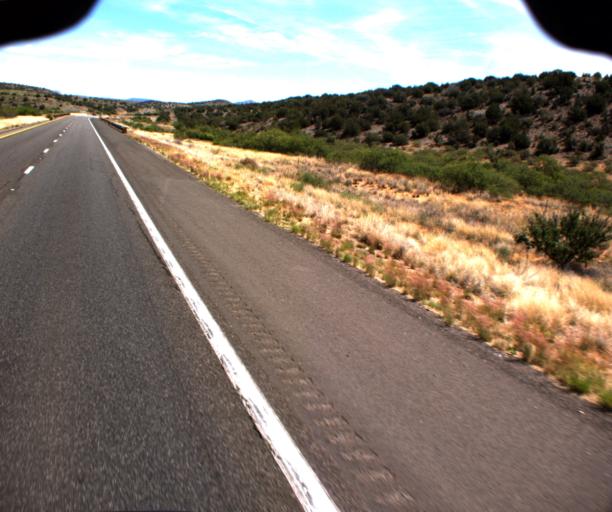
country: US
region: Arizona
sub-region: Yavapai County
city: Cornville
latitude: 34.7808
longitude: -111.9262
